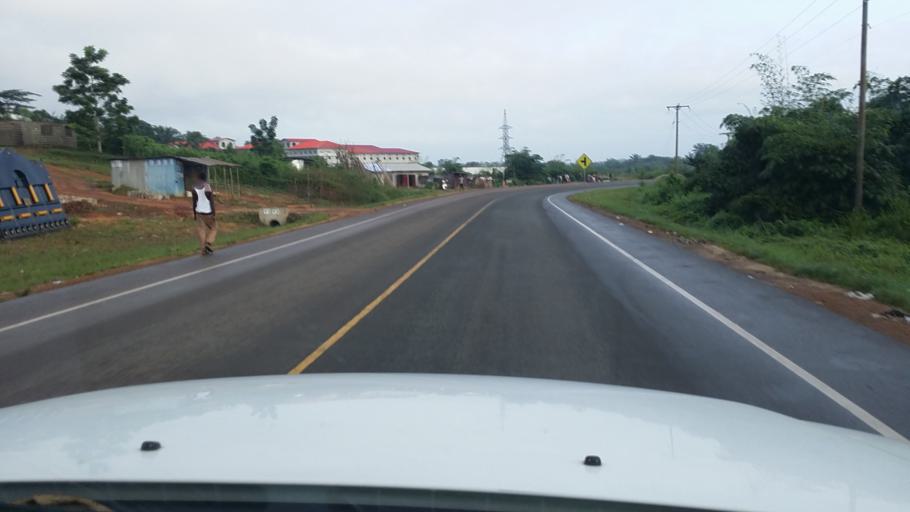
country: LR
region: Montserrado
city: Bensonville City
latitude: 6.3368
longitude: -10.6591
